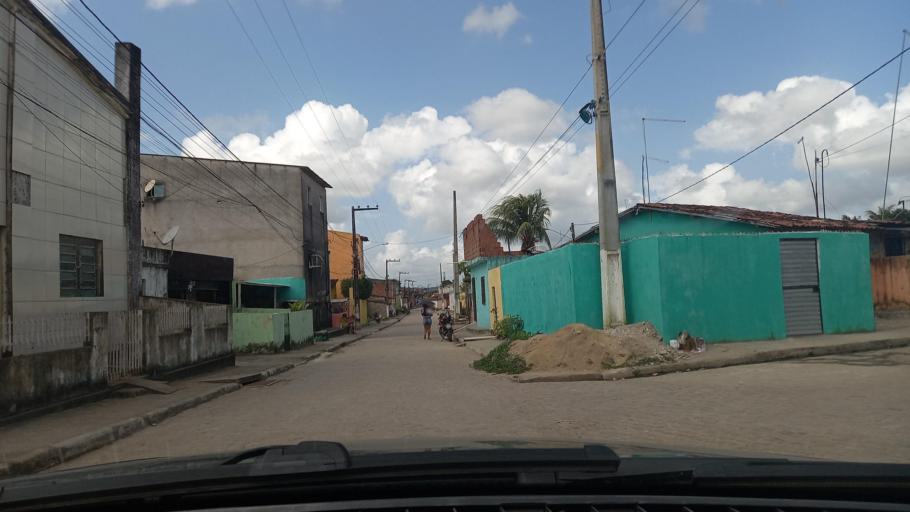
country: BR
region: Pernambuco
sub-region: Goiana
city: Goiana
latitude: -7.5673
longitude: -35.0207
